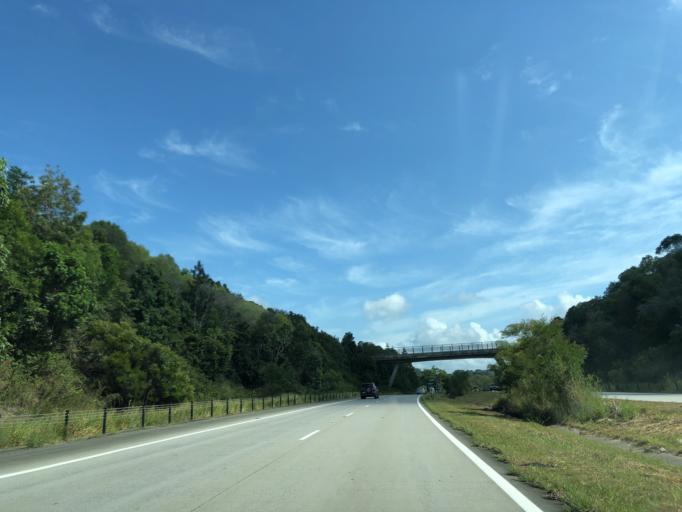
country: AU
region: New South Wales
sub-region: Byron Shire
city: Brunswick Heads
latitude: -28.5741
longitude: 153.5415
